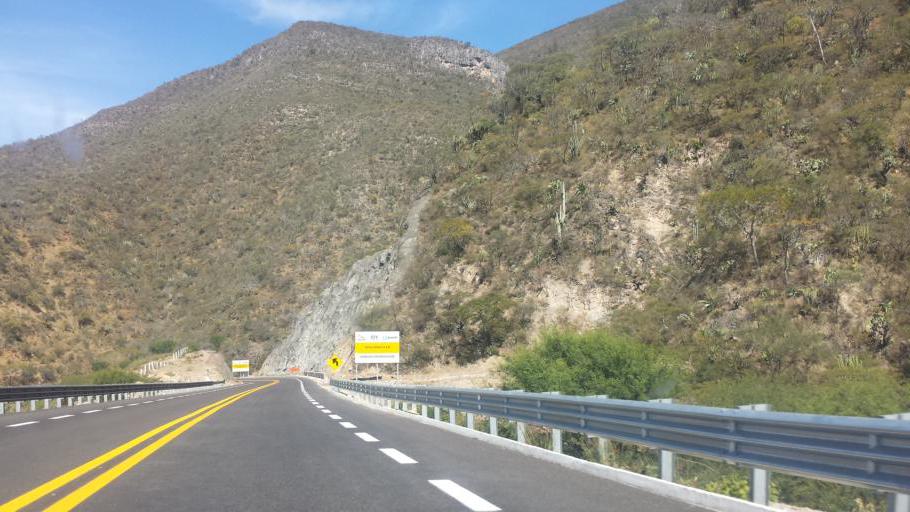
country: MX
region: Puebla
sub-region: San Jose Miahuatlan
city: San Pedro Tetitlan
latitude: 18.1017
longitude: -97.3361
